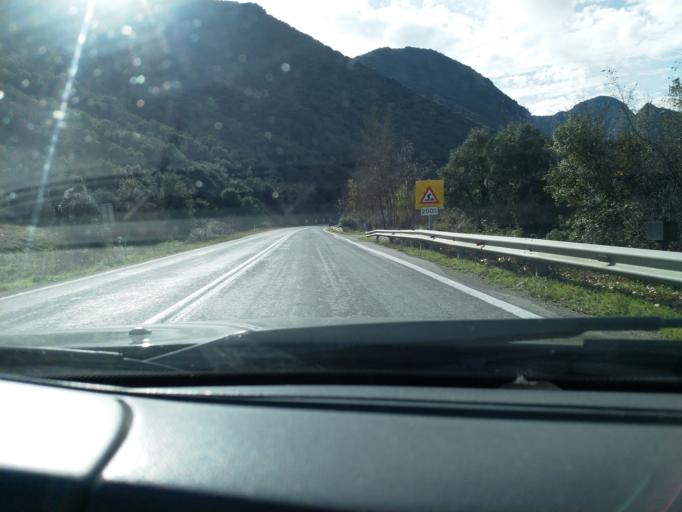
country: GR
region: Epirus
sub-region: Nomos Prevezis
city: Pappadates
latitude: 39.4141
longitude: 20.8443
